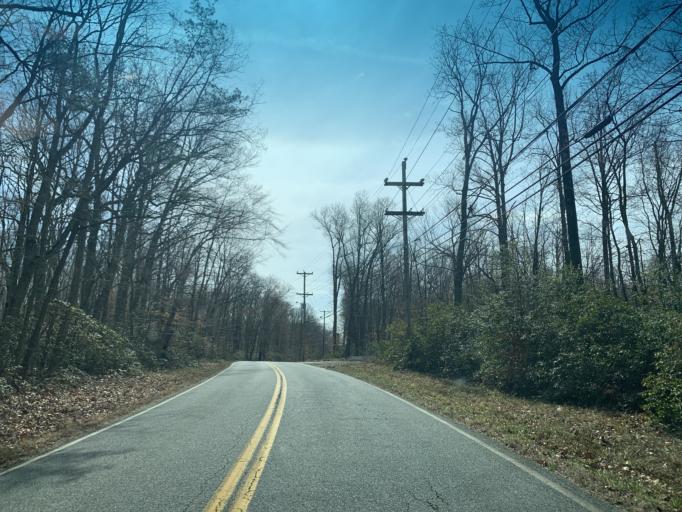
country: US
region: Maryland
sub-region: Cecil County
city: Charlestown
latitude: 39.5647
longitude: -76.0216
